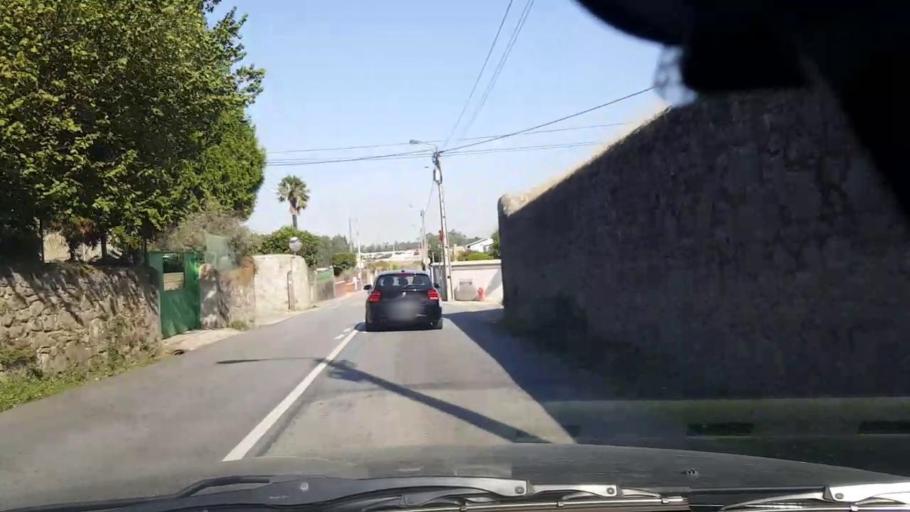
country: PT
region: Porto
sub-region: Vila do Conde
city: Arvore
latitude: 41.3321
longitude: -8.6809
